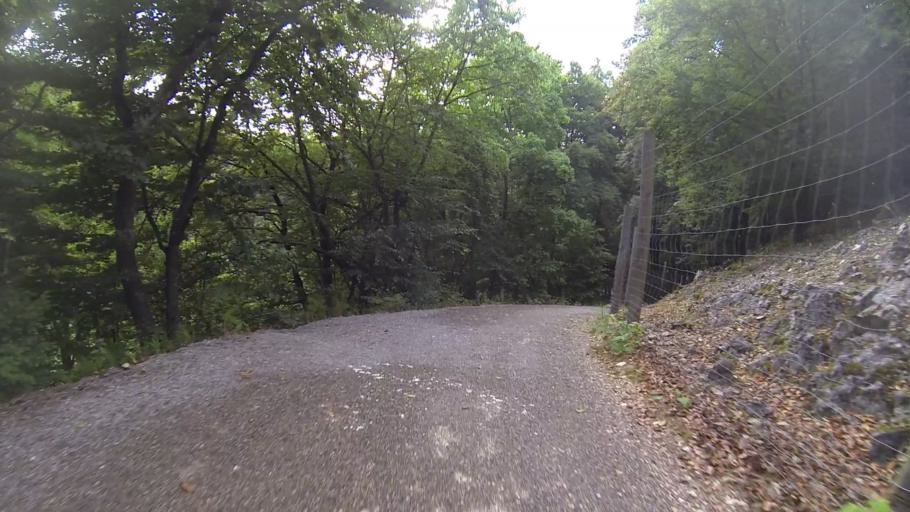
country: DE
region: Baden-Wuerttemberg
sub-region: Regierungsbezirk Stuttgart
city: Heidenheim an der Brenz
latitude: 48.6694
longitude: 10.1347
